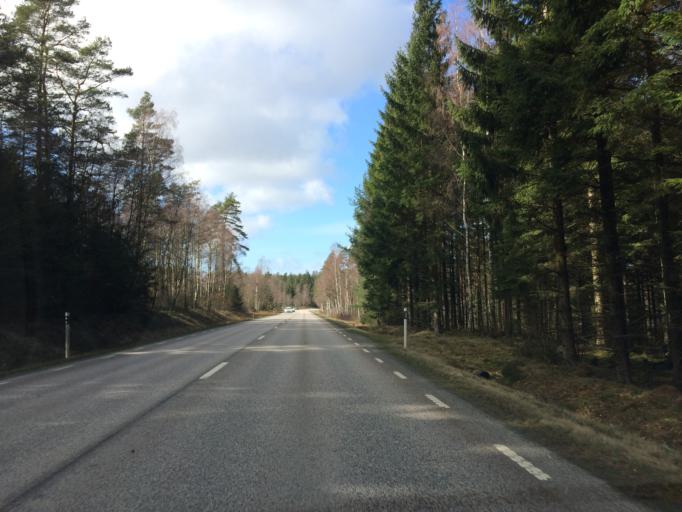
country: SE
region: Halland
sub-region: Laholms Kommun
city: Knared
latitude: 56.4934
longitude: 13.3912
